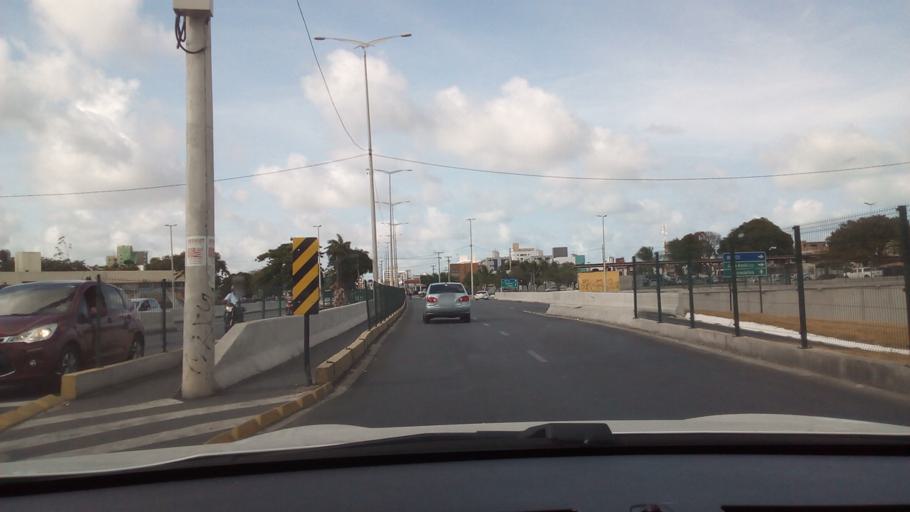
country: BR
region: Paraiba
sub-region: Joao Pessoa
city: Joao Pessoa
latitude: -7.1623
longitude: -34.8384
